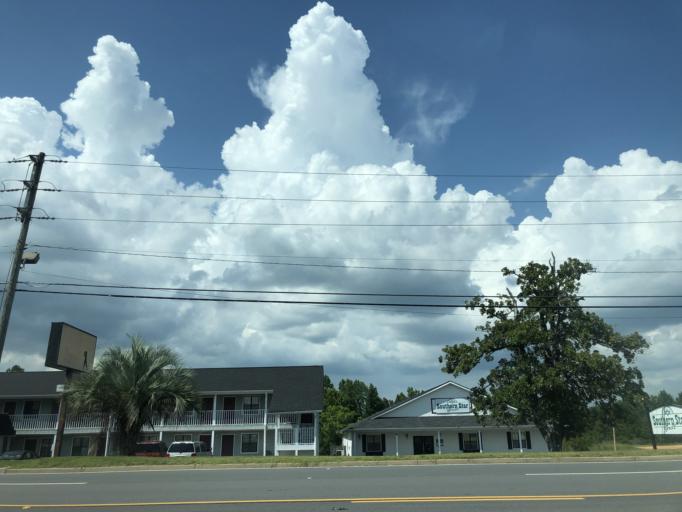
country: US
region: Georgia
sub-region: Telfair County
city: McRae
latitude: 32.0634
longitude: -82.8858
